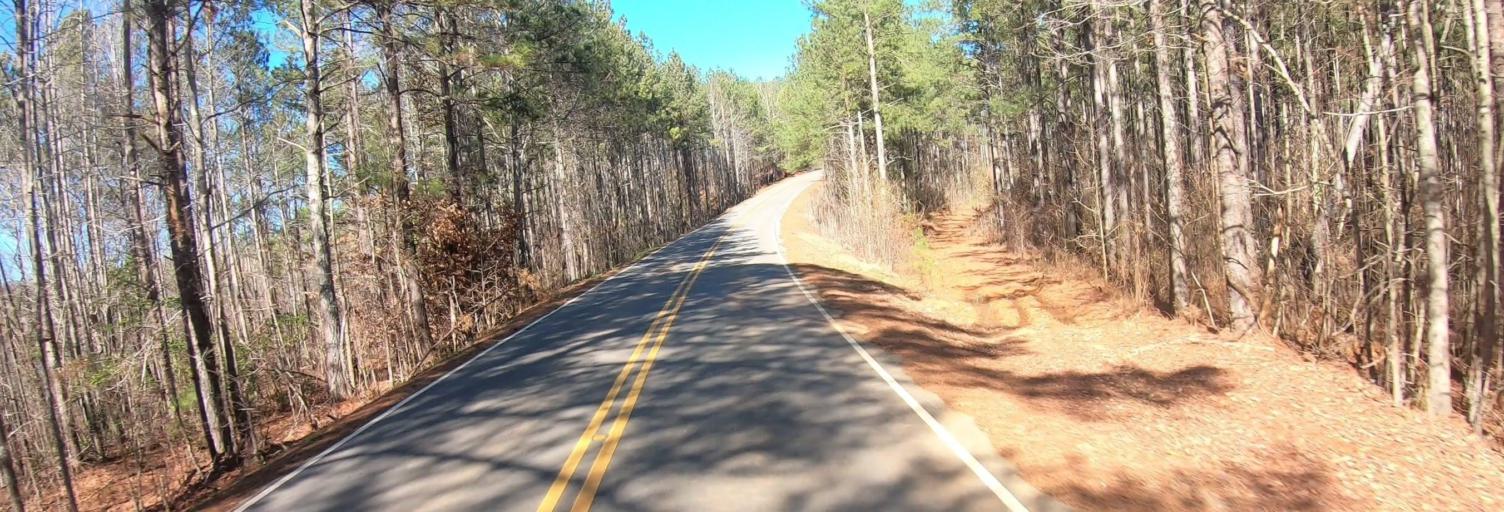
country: US
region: Alabama
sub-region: Clay County
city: Ashland
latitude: 33.3788
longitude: -85.8717
